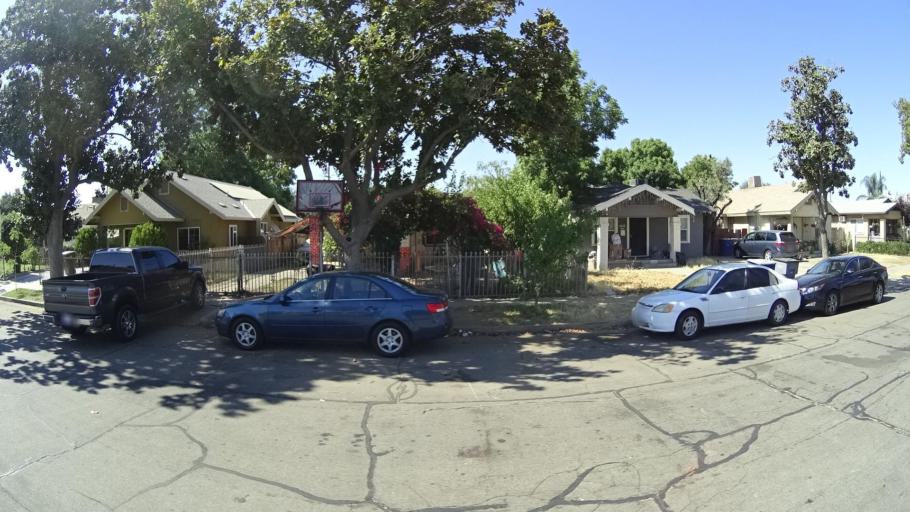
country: US
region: California
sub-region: Fresno County
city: Fresno
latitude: 36.7328
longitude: -119.7665
